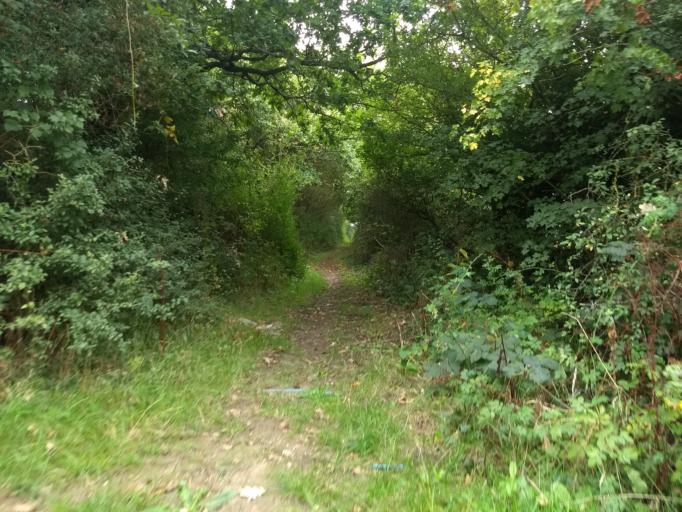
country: GB
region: England
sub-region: Isle of Wight
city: Newport
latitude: 50.7099
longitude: -1.2758
